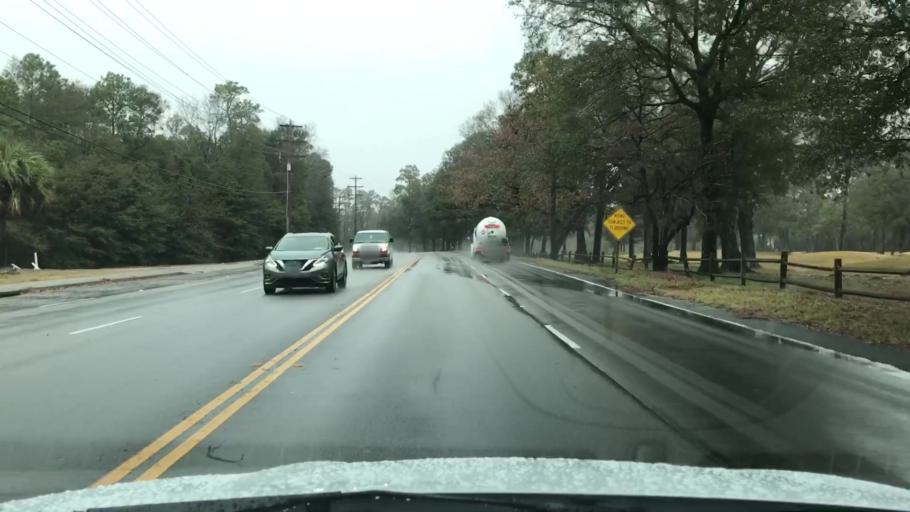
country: US
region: South Carolina
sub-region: Horry County
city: North Myrtle Beach
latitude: 33.7706
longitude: -78.7893
